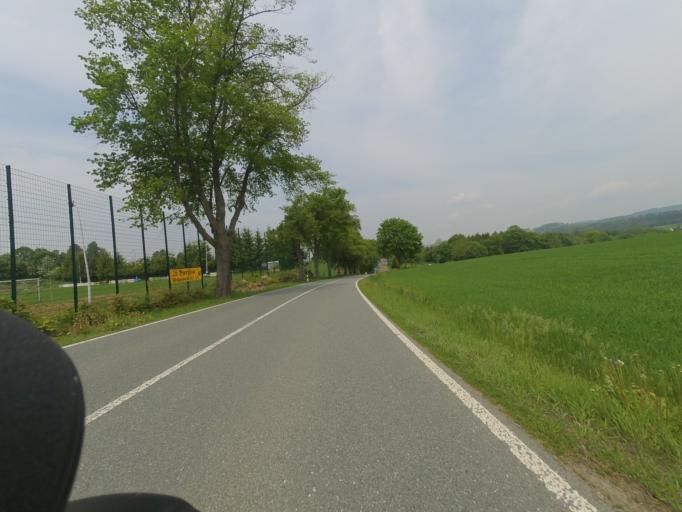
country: DE
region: Saxony
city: Wolkenstein
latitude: 50.6542
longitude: 13.0792
